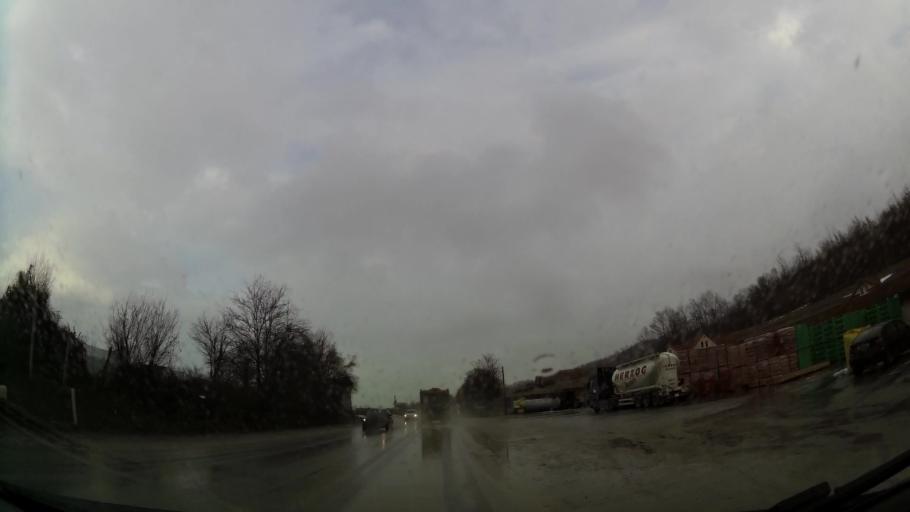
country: XK
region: Ferizaj
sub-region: Komuna e Kacanikut
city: Kacanik
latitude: 42.2441
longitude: 21.2414
